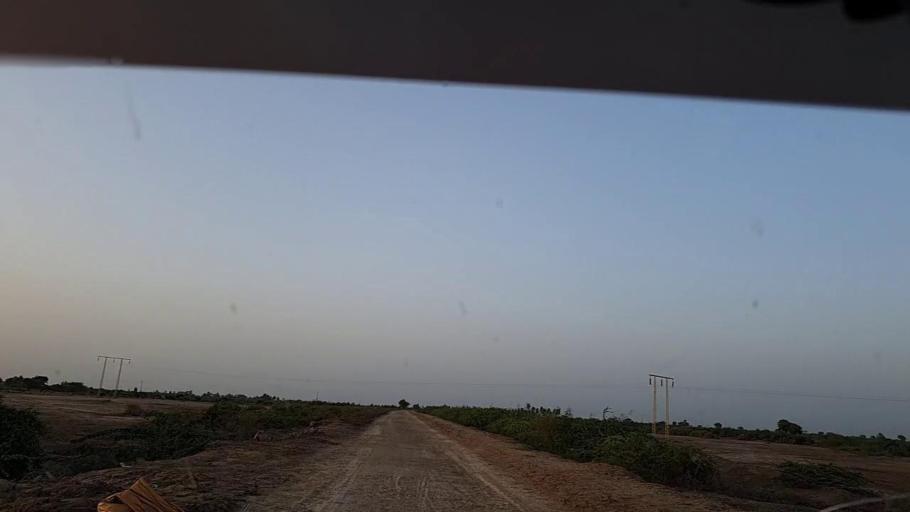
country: PK
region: Sindh
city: Kadhan
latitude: 24.5250
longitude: 68.9435
